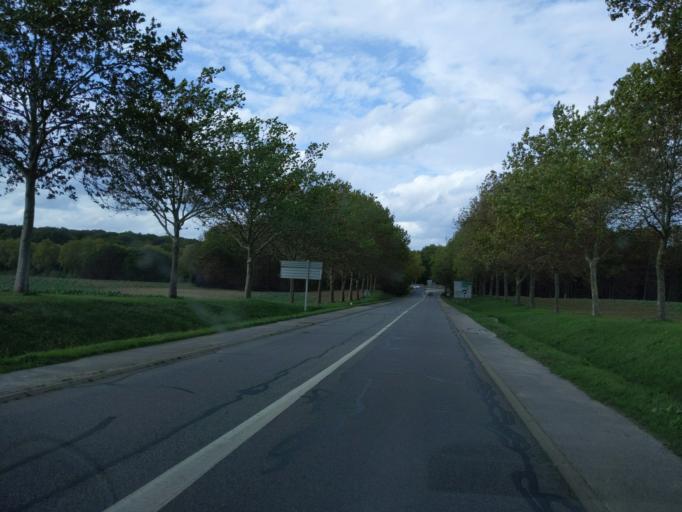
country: FR
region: Ile-de-France
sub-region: Departement des Yvelines
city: Rambouillet
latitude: 48.6599
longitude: 1.8341
